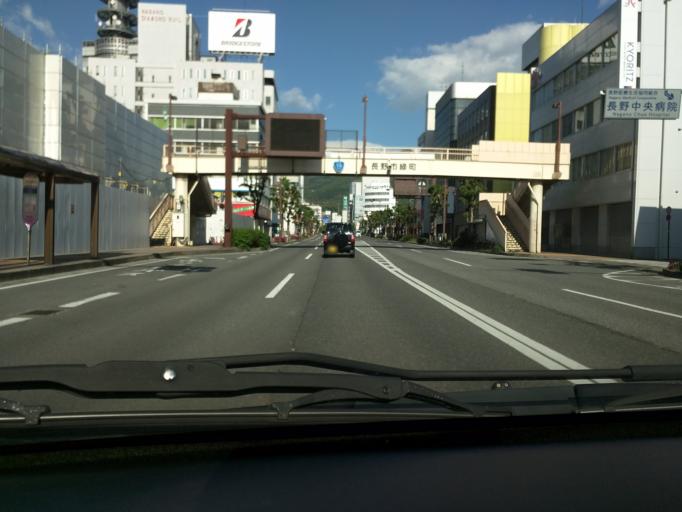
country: JP
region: Nagano
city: Nagano-shi
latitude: 36.6489
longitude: 138.1948
